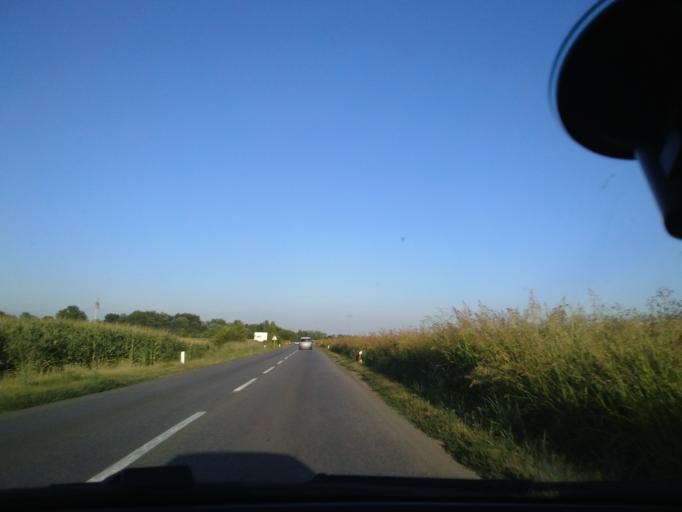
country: RS
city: Kisac
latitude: 45.3353
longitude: 19.6713
